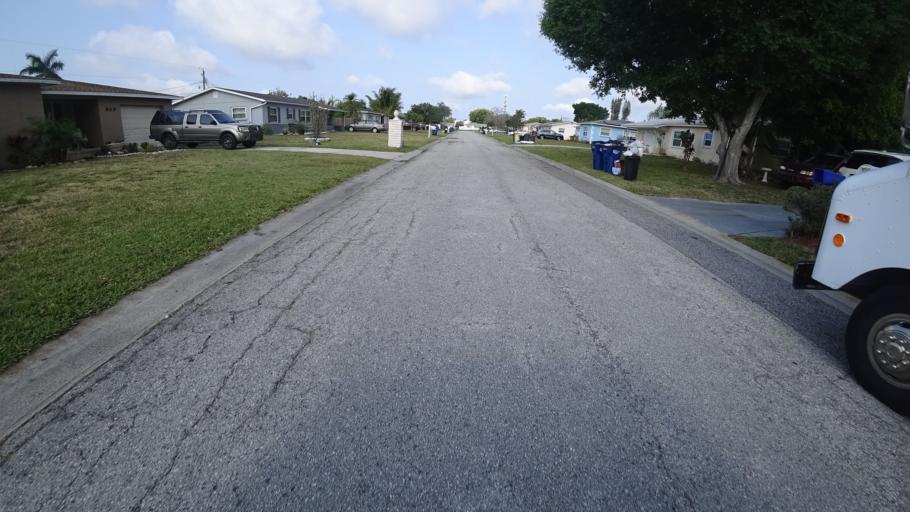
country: US
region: Florida
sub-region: Manatee County
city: South Bradenton
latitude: 27.4577
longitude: -82.5708
